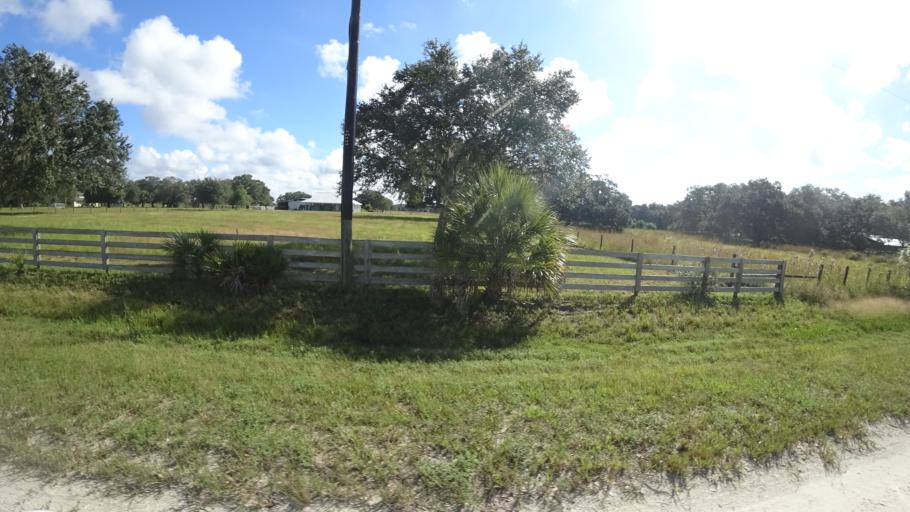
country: US
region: Florida
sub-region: Sarasota County
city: Lake Sarasota
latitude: 27.3182
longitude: -82.2196
